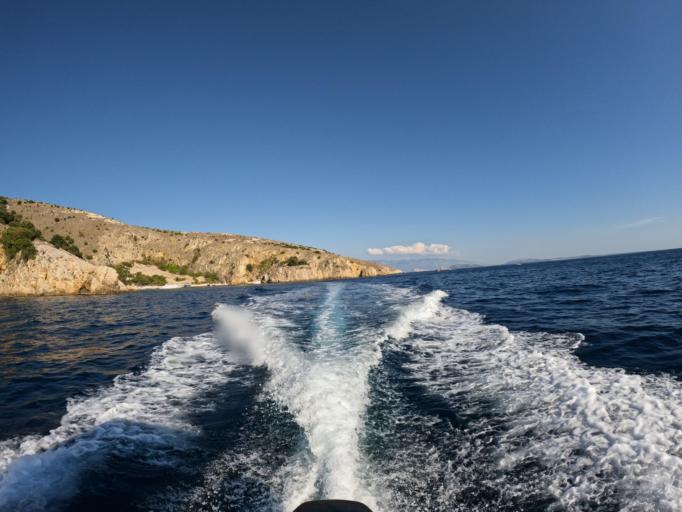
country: HR
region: Primorsko-Goranska
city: Punat
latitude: 44.9731
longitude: 14.6327
